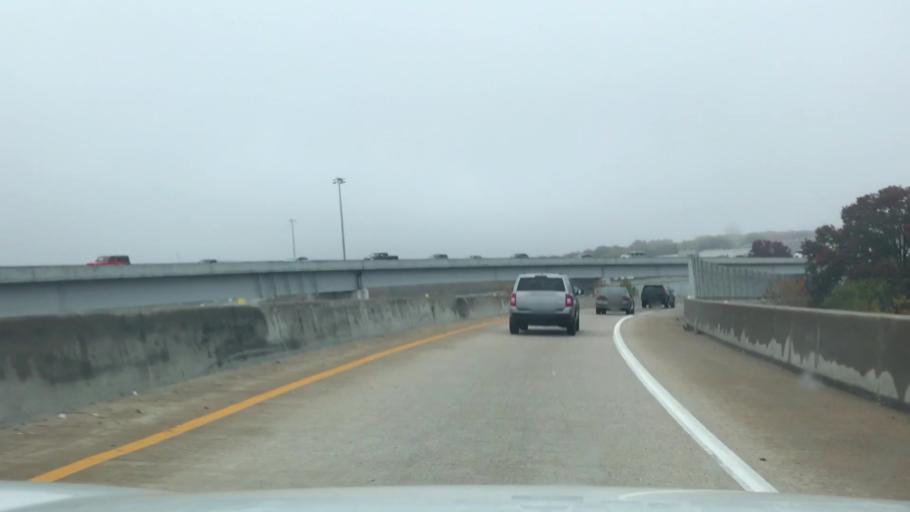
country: US
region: Missouri
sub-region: Saint Louis County
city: Brentwood
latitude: 38.6303
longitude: -90.3427
